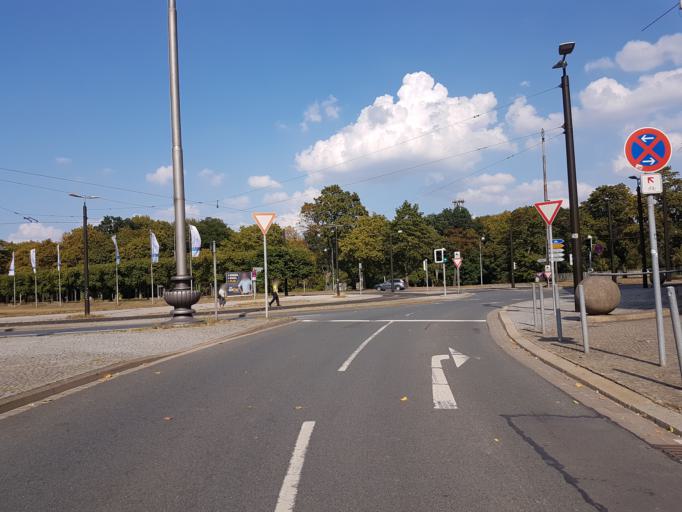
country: DE
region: Lower Saxony
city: Hannover
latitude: 52.3763
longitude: 9.7686
